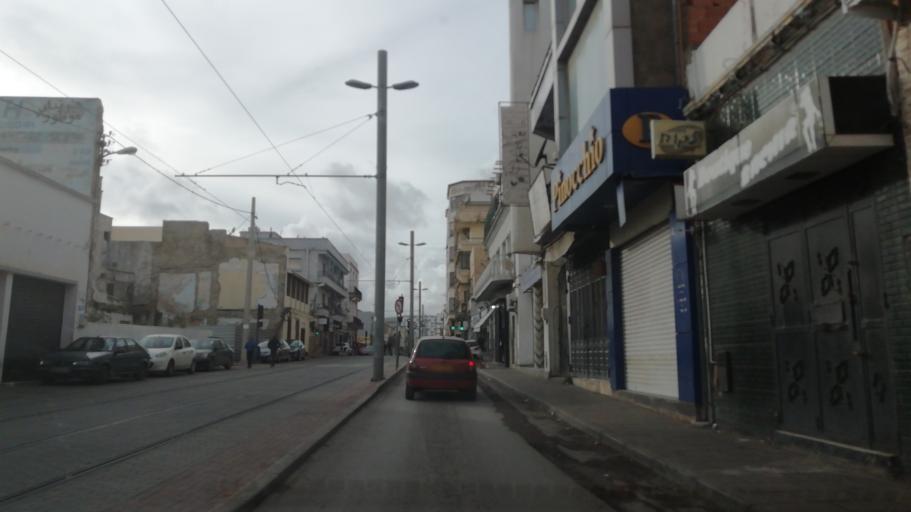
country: DZ
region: Oran
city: Oran
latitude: 35.6987
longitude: -0.6213
